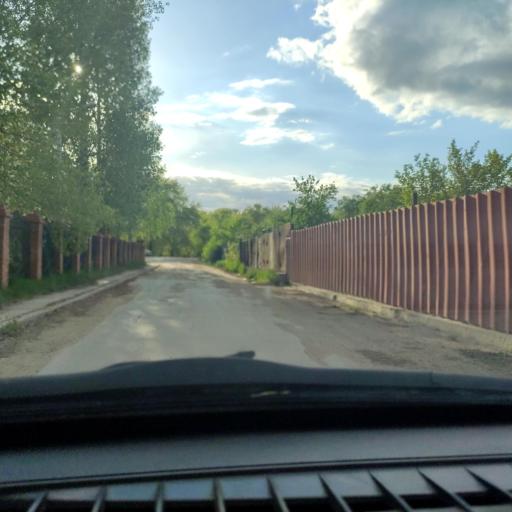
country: RU
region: Samara
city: Zhigulevsk
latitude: 53.4498
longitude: 49.5361
